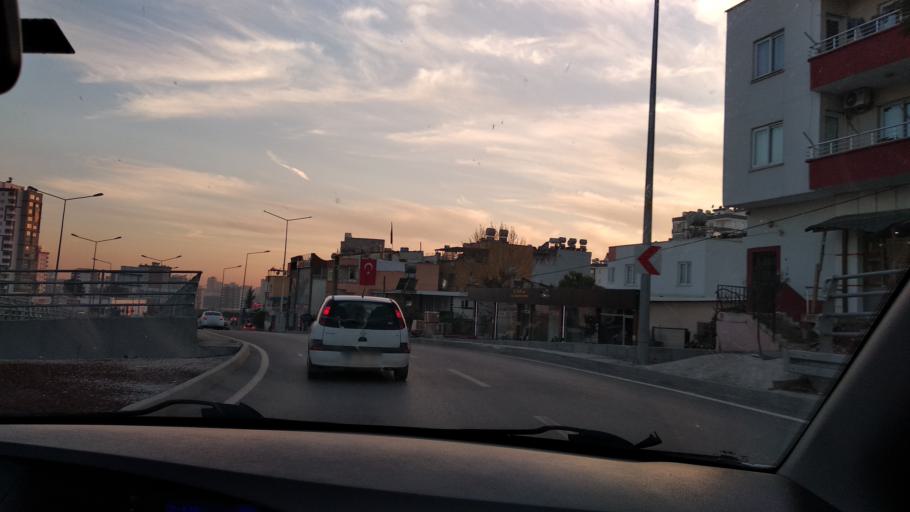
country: TR
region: Mersin
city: Mercin
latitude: 36.8195
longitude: 34.5967
